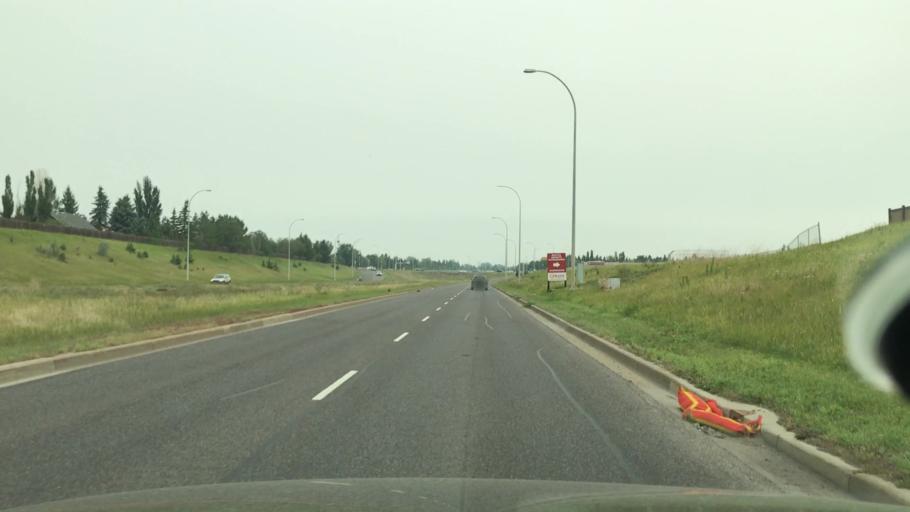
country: CA
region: Alberta
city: Edmonton
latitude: 53.4721
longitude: -113.5783
